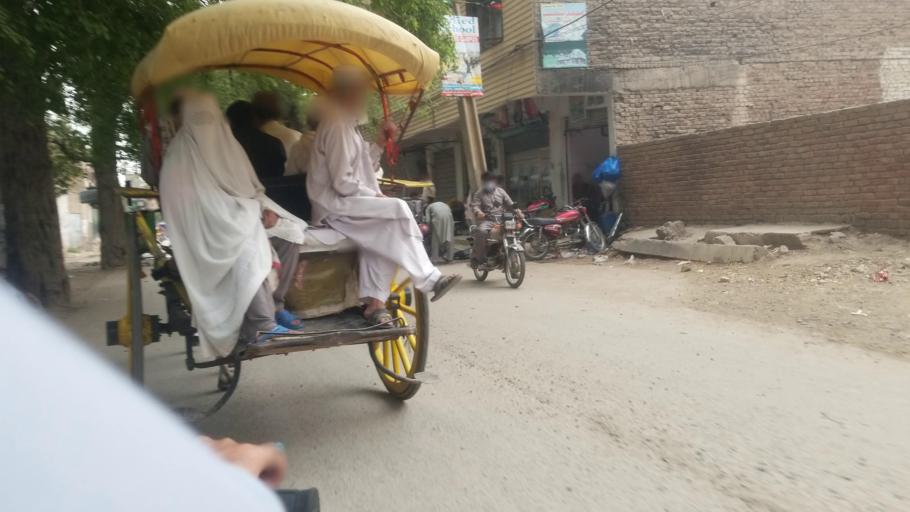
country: PK
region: Khyber Pakhtunkhwa
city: Peshawar
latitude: 33.9911
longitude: 71.5545
